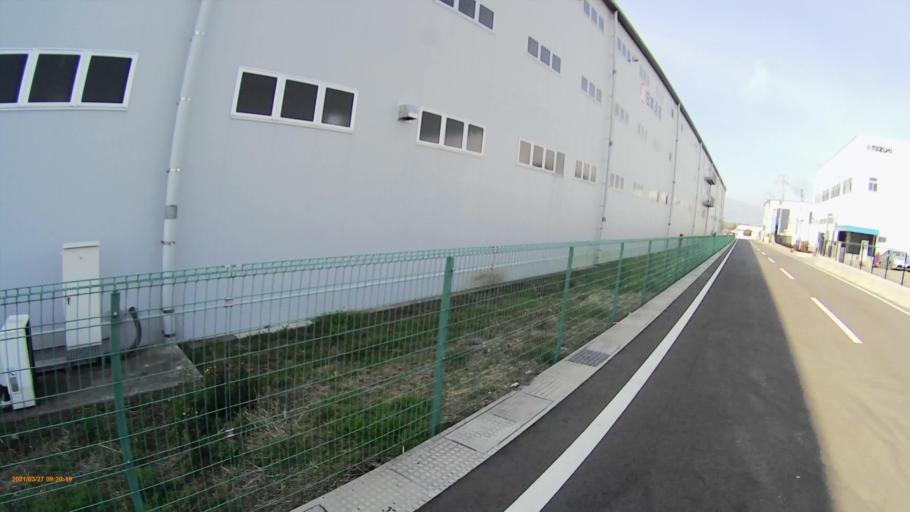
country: JP
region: Kanagawa
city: Minami-rinkan
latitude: 35.4462
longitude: 139.4190
